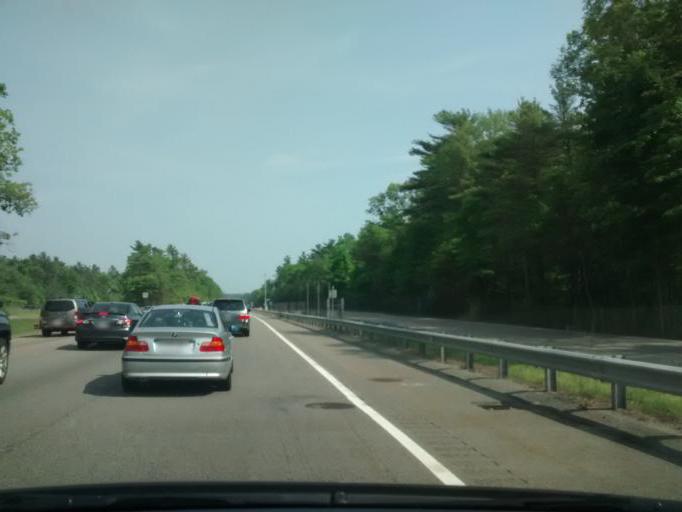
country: US
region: Massachusetts
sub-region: Bristol County
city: Raynham Center
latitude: 41.9337
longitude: -71.0092
